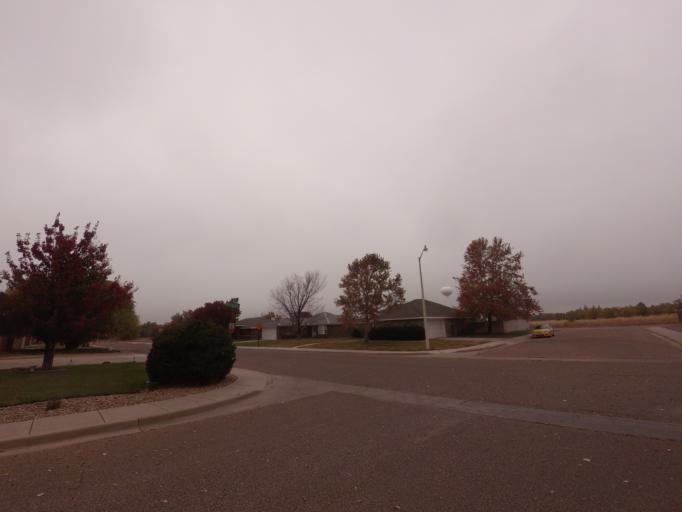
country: US
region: New Mexico
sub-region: Curry County
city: Clovis
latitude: 34.4278
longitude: -103.1854
